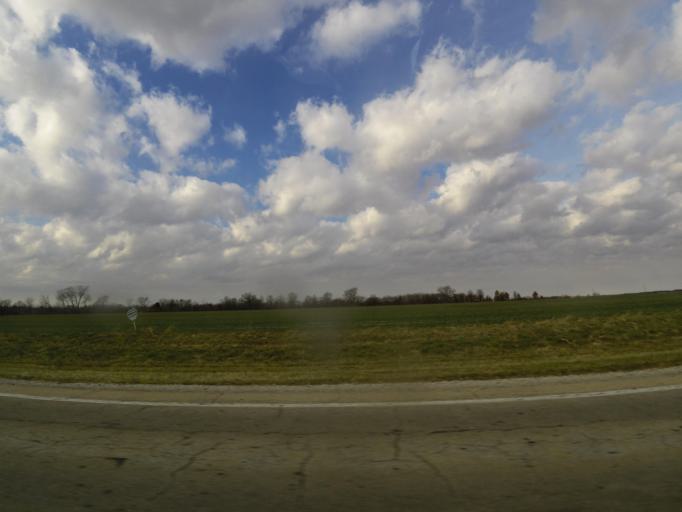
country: US
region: Illinois
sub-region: Fayette County
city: Ramsey
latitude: 39.2000
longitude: -89.1009
